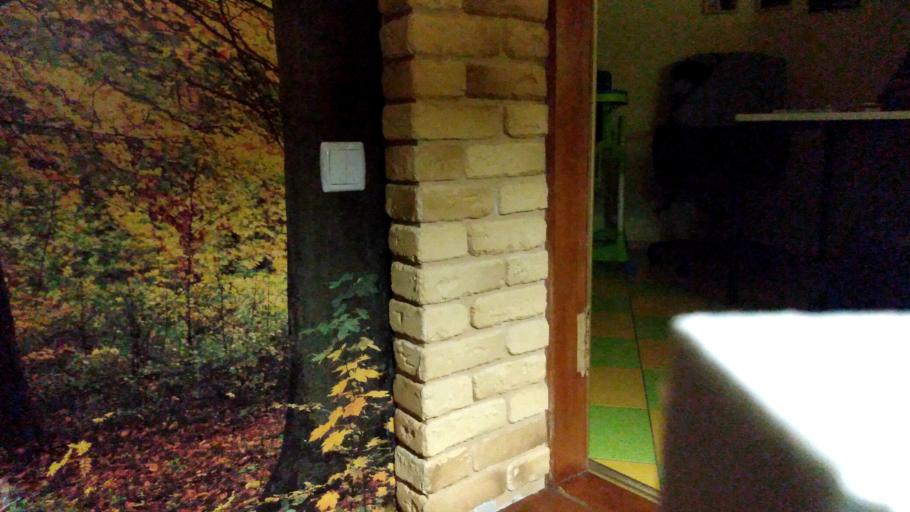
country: RU
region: Vologda
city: Lipin Bor
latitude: 60.7474
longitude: 38.0521
